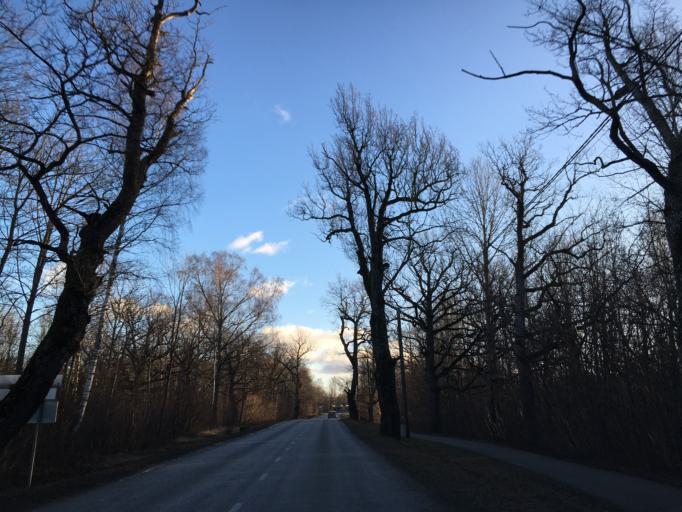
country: EE
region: Harju
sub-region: Saue linn
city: Saue
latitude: 59.3187
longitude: 24.5547
